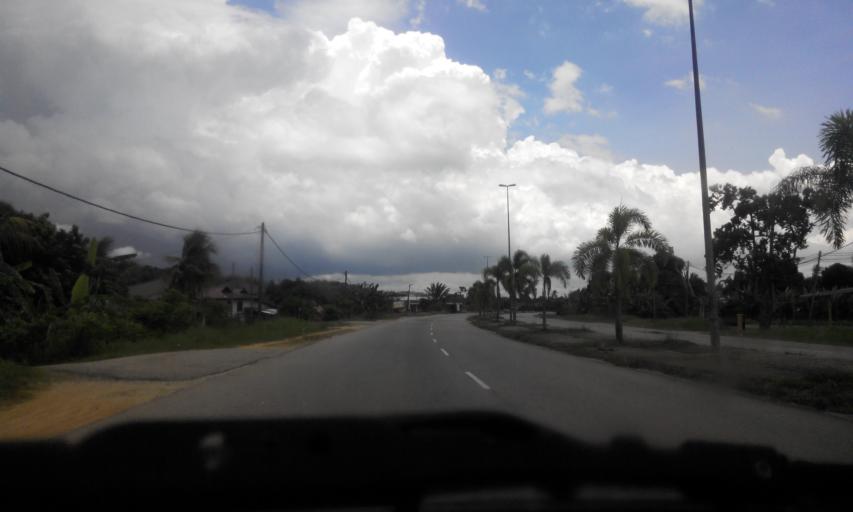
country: MY
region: Perak
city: Parit Buntar
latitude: 5.1277
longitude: 100.5109
